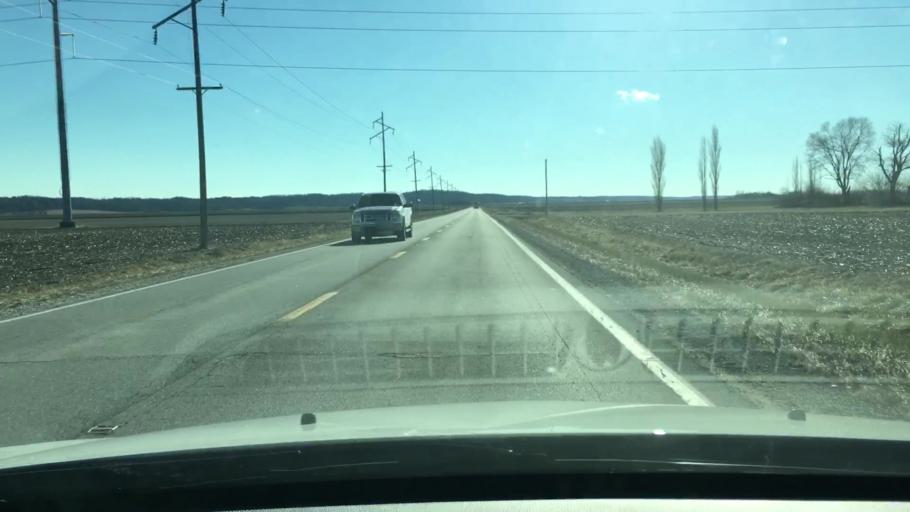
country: US
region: Illinois
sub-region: Morgan County
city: Meredosia
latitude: 39.8630
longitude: -90.5054
